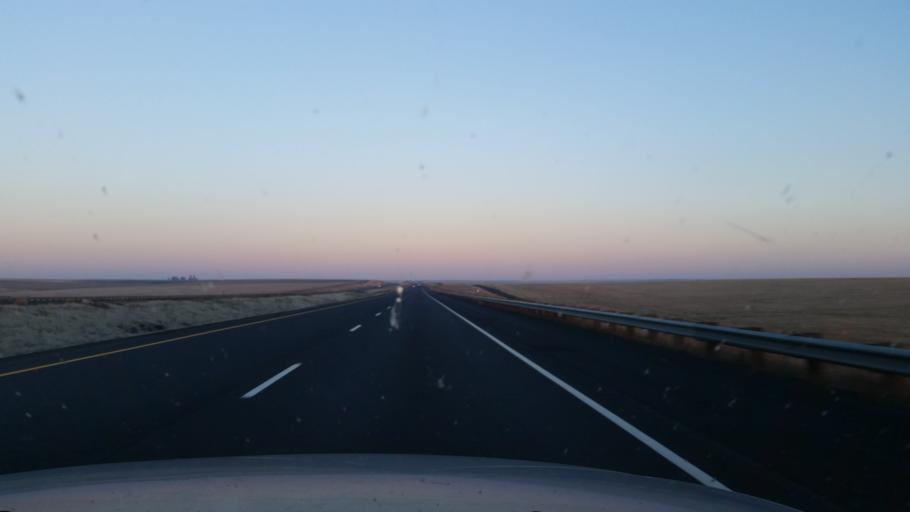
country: US
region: Washington
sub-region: Grant County
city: Warden
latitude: 47.0859
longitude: -118.8047
